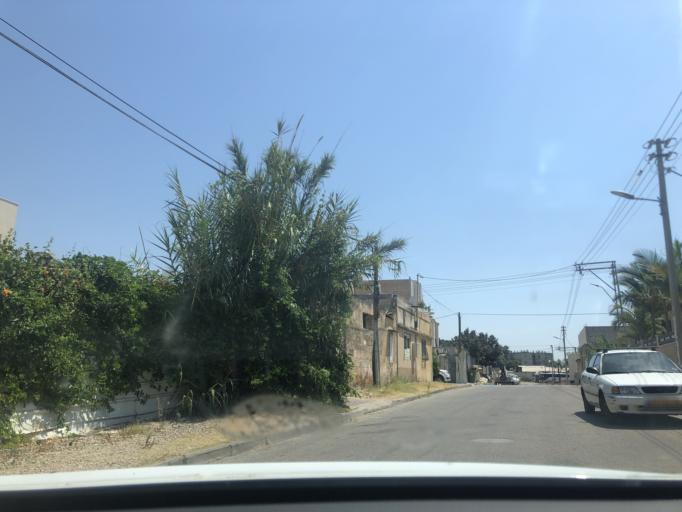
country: IL
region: Central District
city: Lod
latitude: 31.9583
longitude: 34.9006
